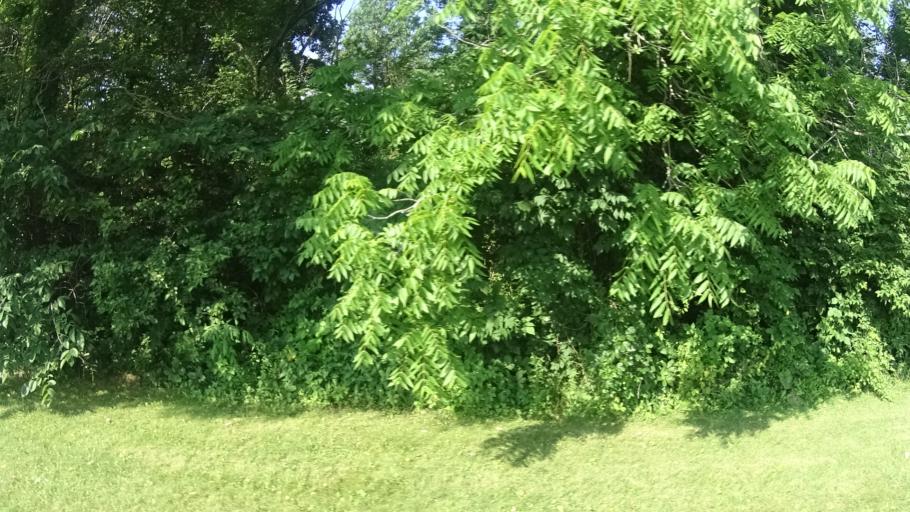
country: US
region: Ohio
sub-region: Lorain County
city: Vermilion
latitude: 41.3886
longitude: -82.4410
